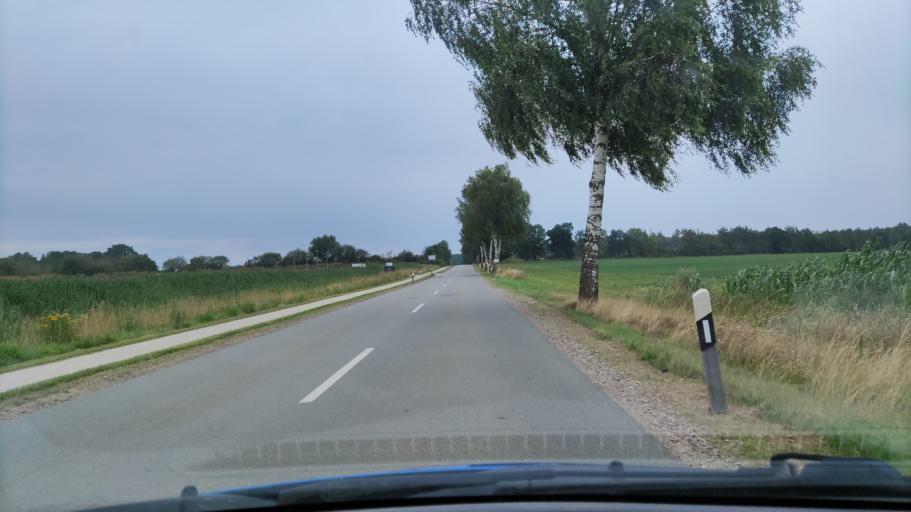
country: DE
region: Lower Saxony
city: Rosche
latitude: 52.9908
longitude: 10.7646
